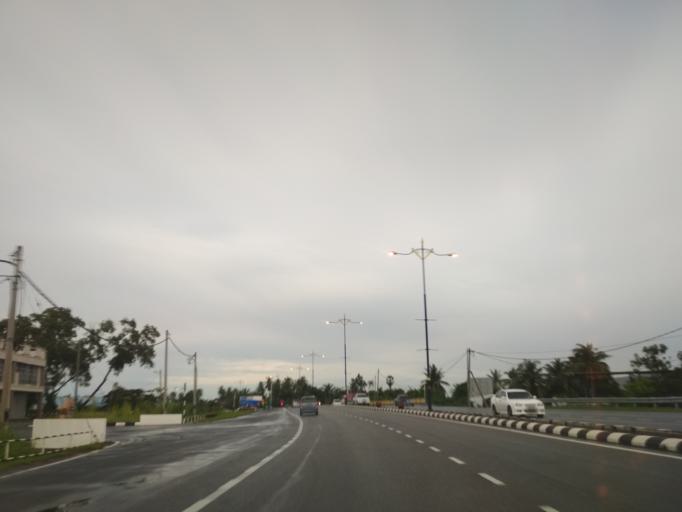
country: MY
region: Perlis
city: Kangar
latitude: 6.4334
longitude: 100.1996
